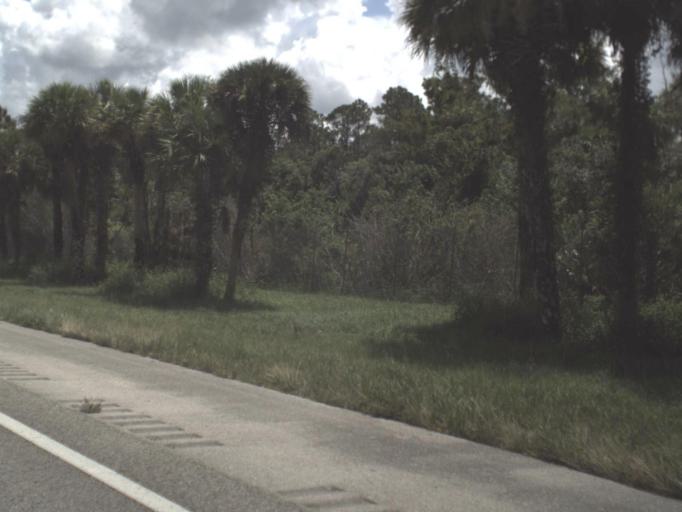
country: US
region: Florida
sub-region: Collier County
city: Orangetree
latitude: 26.1530
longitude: -81.4819
